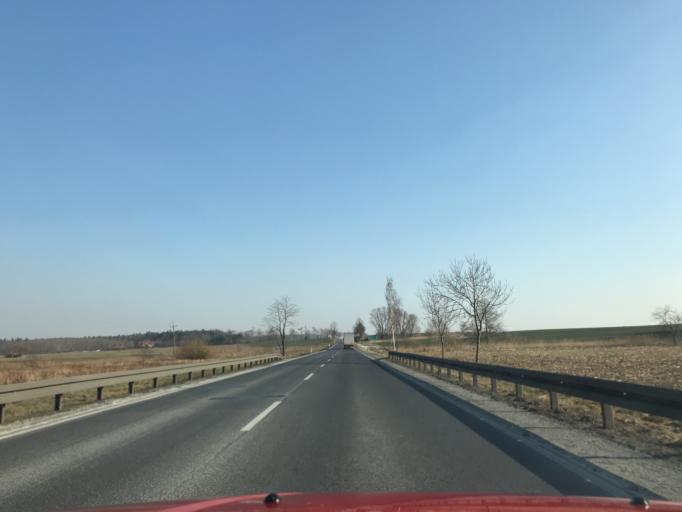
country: PL
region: Greater Poland Voivodeship
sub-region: Powiat sredzki
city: Nowe Miasto nad Warta
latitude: 52.0829
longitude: 17.4040
